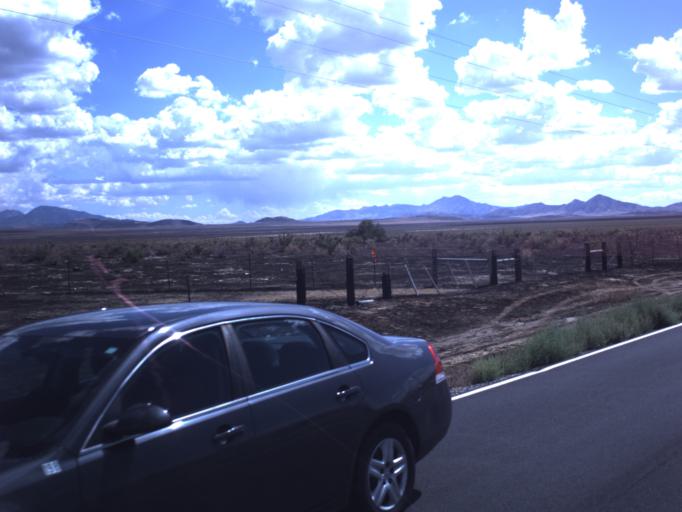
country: US
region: Utah
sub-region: Tooele County
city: Grantsville
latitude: 40.2885
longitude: -112.6619
